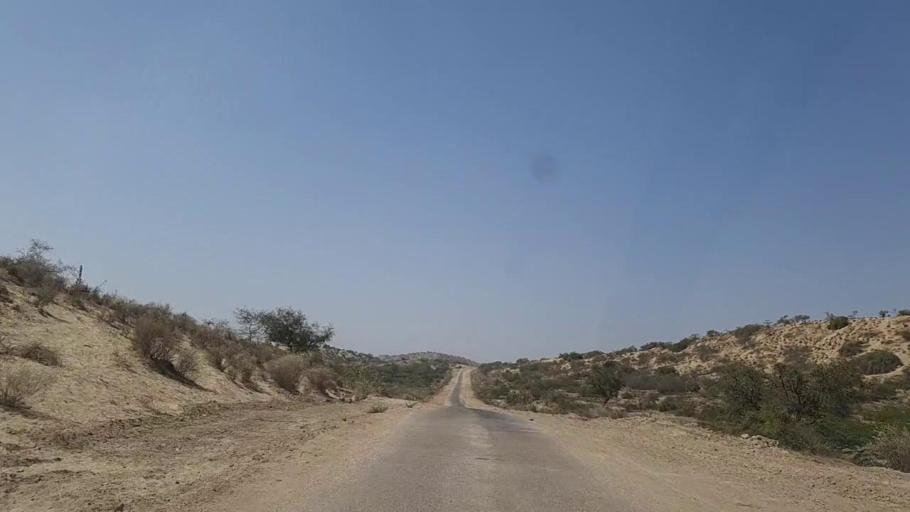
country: PK
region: Sindh
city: Diplo
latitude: 24.5406
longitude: 69.4074
